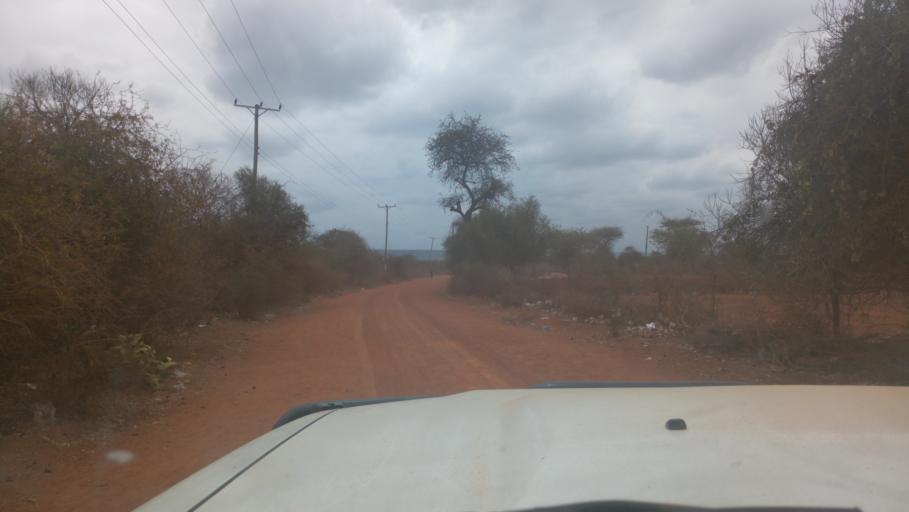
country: KE
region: Makueni
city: Wote
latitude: -1.6661
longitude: 37.8936
